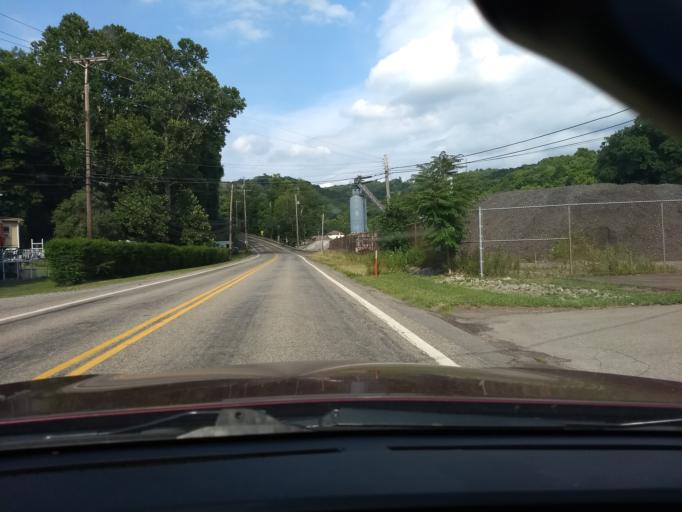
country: US
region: Pennsylvania
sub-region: Allegheny County
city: Bell Acres
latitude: 40.5966
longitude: -80.1903
